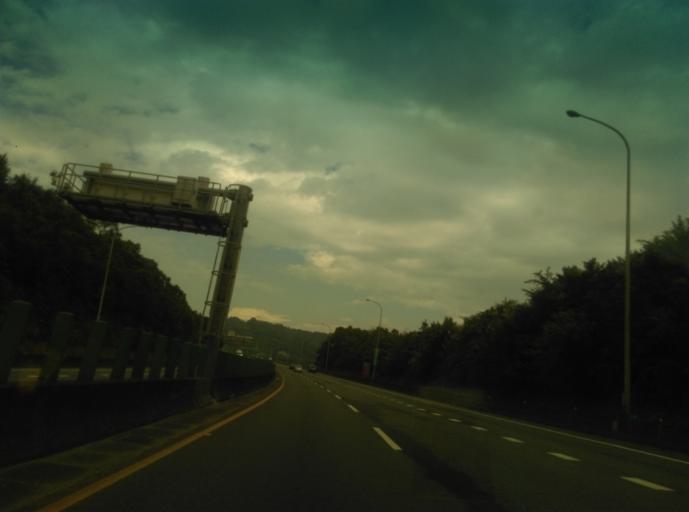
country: TW
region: Taiwan
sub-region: Keelung
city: Keelung
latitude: 25.1185
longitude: 121.6966
